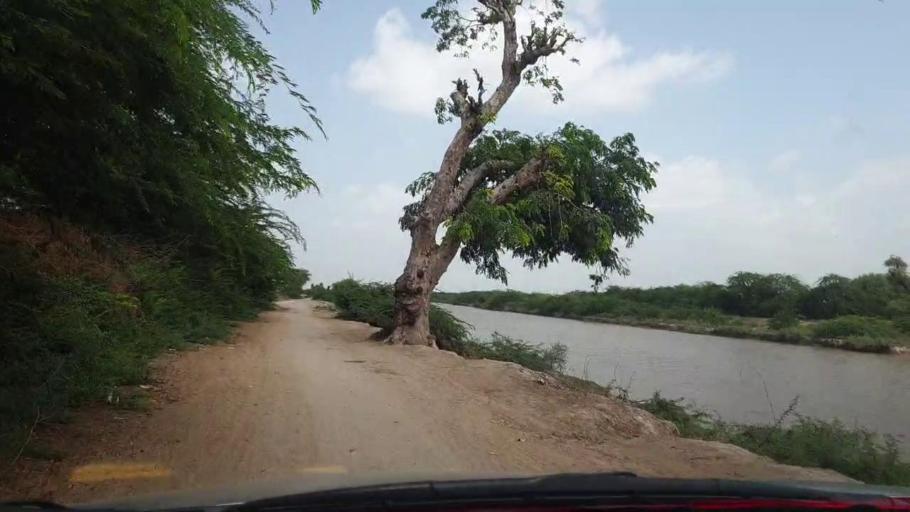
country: PK
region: Sindh
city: Talhar
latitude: 24.8883
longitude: 68.8349
